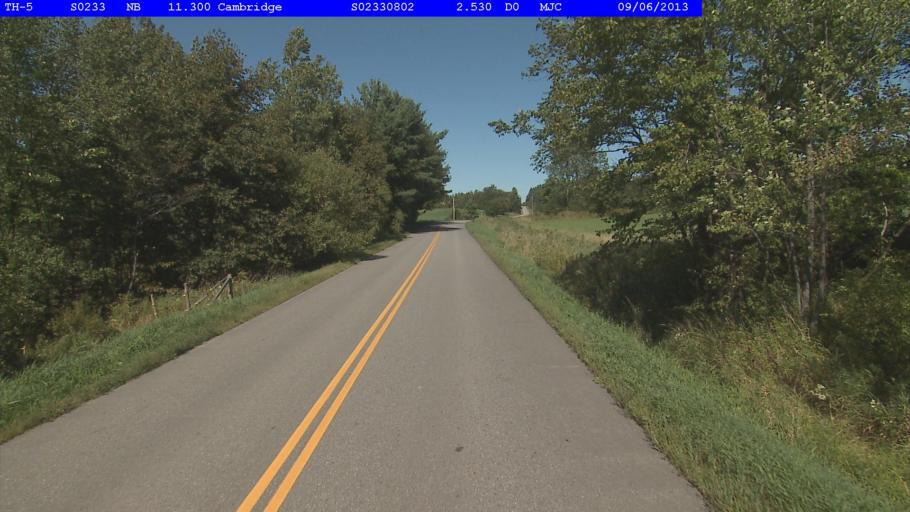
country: US
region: Vermont
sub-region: Lamoille County
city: Johnson
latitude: 44.6181
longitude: -72.8574
